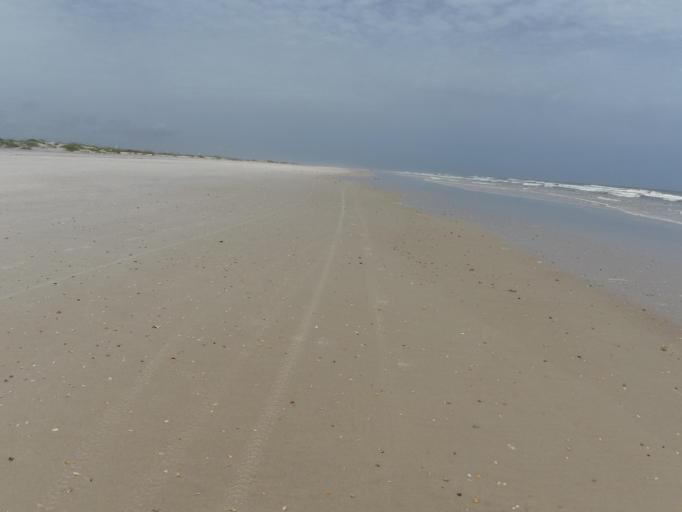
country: US
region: Florida
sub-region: Saint Johns County
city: Saint Augustine
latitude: 29.8990
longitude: -81.2765
